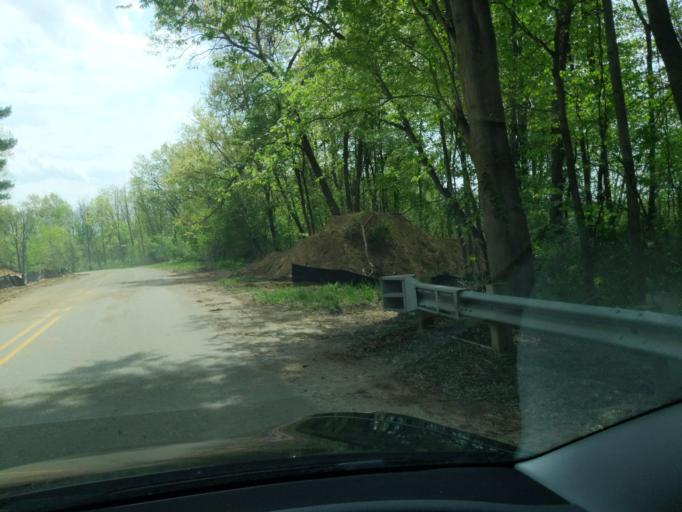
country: US
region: Michigan
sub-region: Ingham County
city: Stockbridge
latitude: 42.4361
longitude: -84.0755
